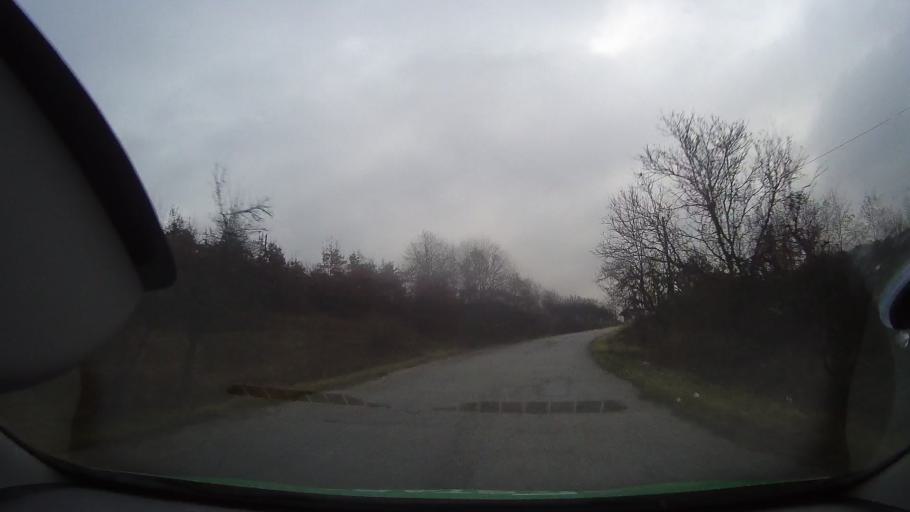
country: RO
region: Hunedoara
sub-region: Comuna Ribita
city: Ribita
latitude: 46.2313
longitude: 22.7398
